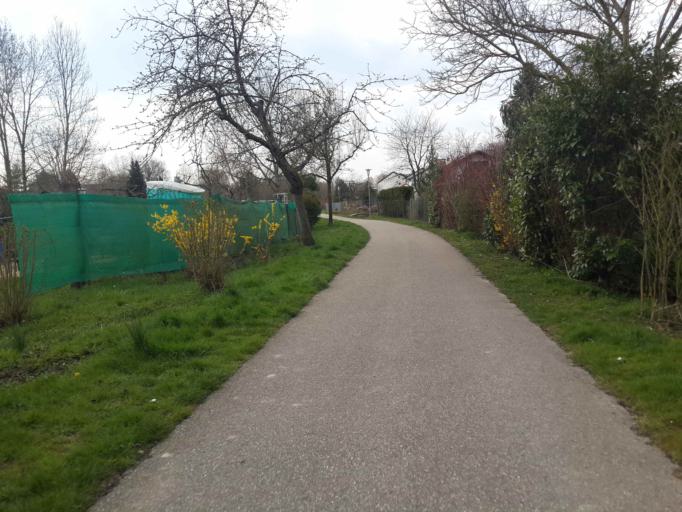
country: DE
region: Baden-Wuerttemberg
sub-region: Karlsruhe Region
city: Balzfeld
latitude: 49.2289
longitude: 8.7843
